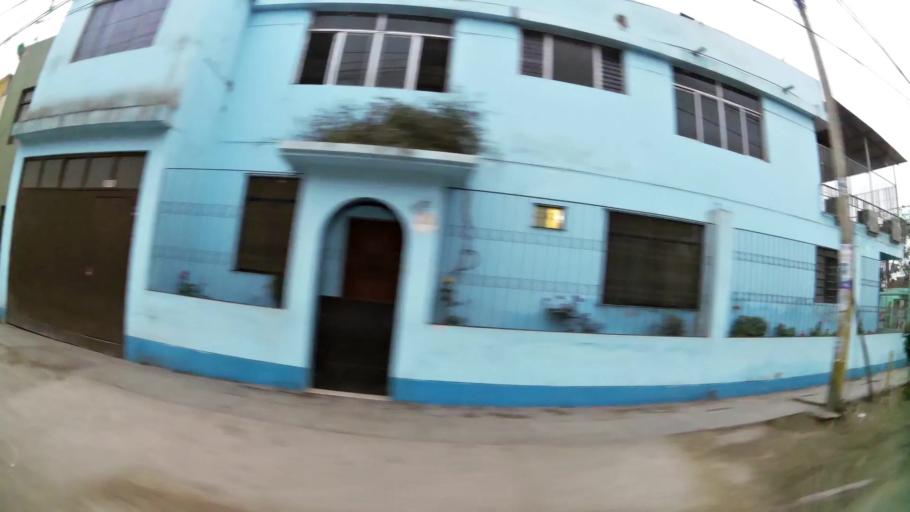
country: PE
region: Lima
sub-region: Lima
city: Surco
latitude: -12.1690
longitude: -76.9722
